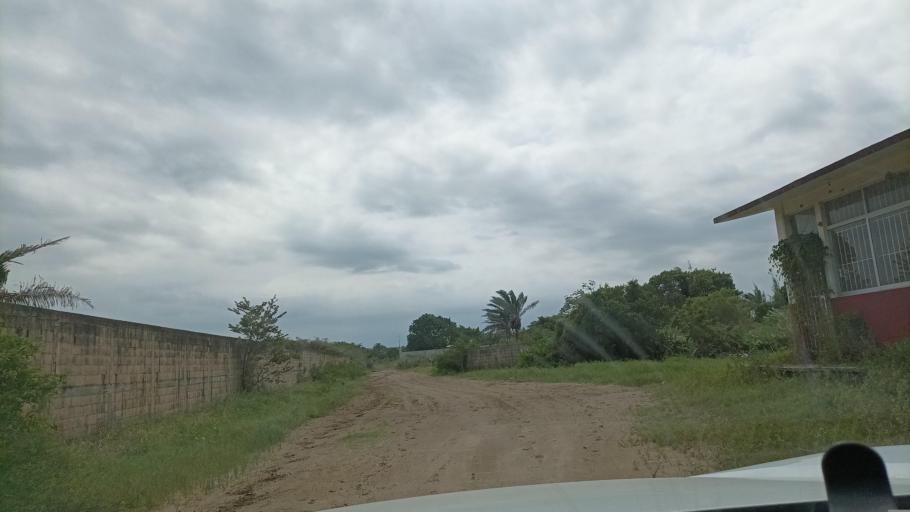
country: MX
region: Veracruz
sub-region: Coatzacoalcos
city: Fraccionamiento Ciudad Olmeca
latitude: 18.1793
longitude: -94.5912
